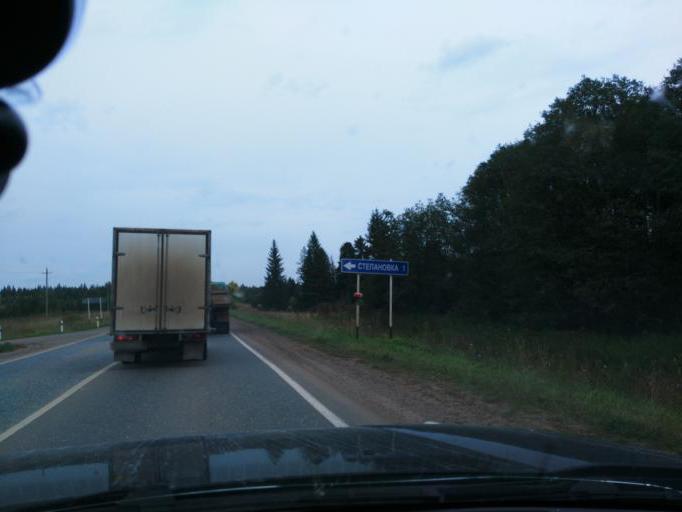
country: RU
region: Perm
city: Chernushka
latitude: 56.5040
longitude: 55.8713
